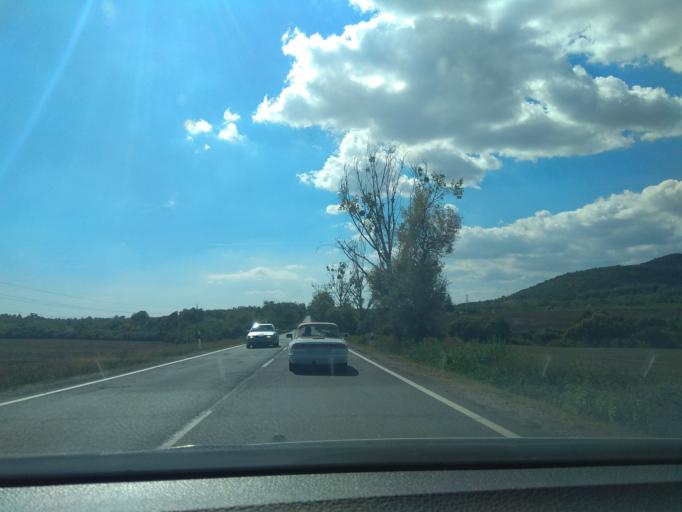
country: HU
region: Borsod-Abauj-Zemplen
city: Sarospatak
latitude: 48.2980
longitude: 21.5158
